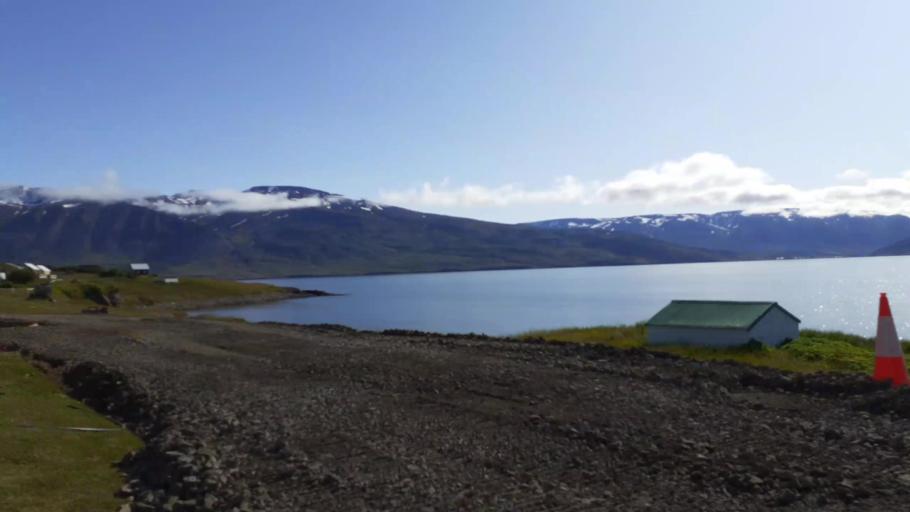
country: IS
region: Northeast
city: Dalvik
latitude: 65.9781
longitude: -18.3655
